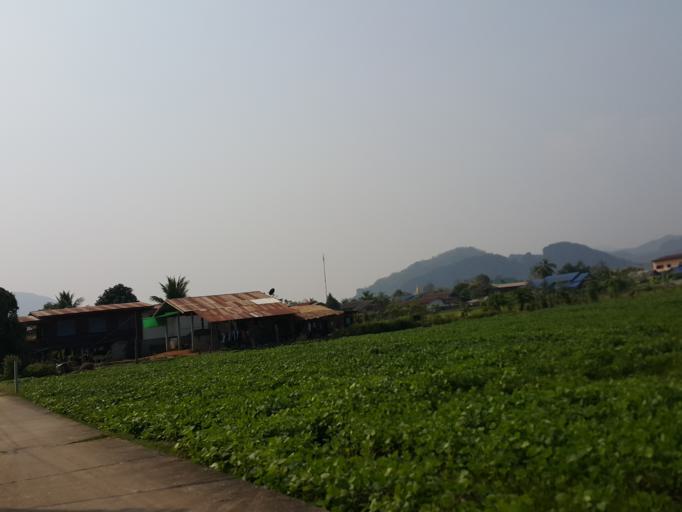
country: TH
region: Sukhothai
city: Thung Saliam
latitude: 17.3251
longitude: 99.5238
